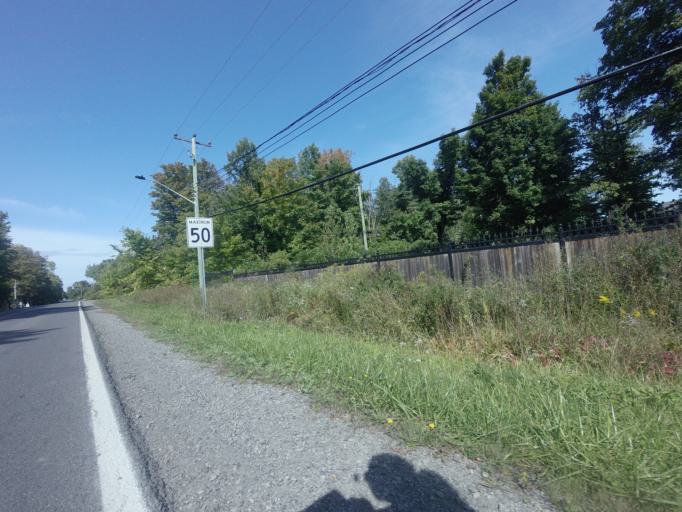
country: CA
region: Quebec
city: Dollard-Des Ormeaux
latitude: 45.5132
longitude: -73.8615
